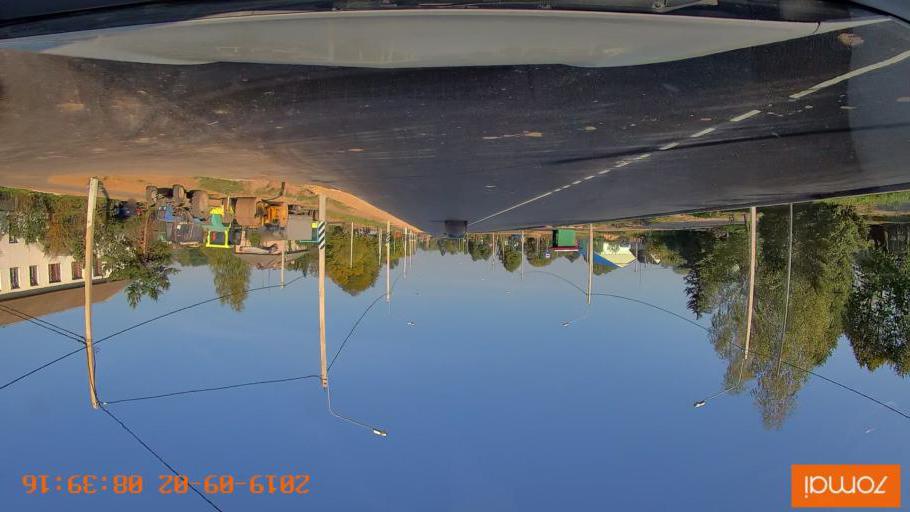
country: RU
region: Kaluga
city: Kudinovo
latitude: 54.9756
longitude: 36.1616
